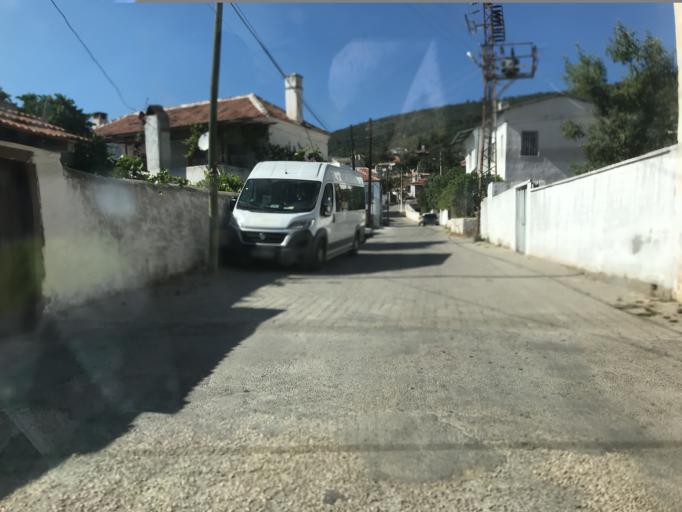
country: TR
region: Mugla
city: Kiulukioi
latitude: 37.3704
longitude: 27.4935
